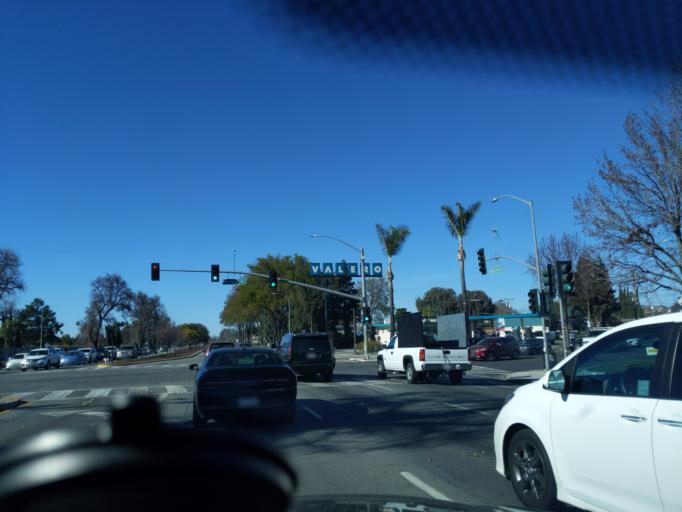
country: US
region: California
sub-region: Santa Clara County
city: Seven Trees
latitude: 37.2602
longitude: -121.8097
